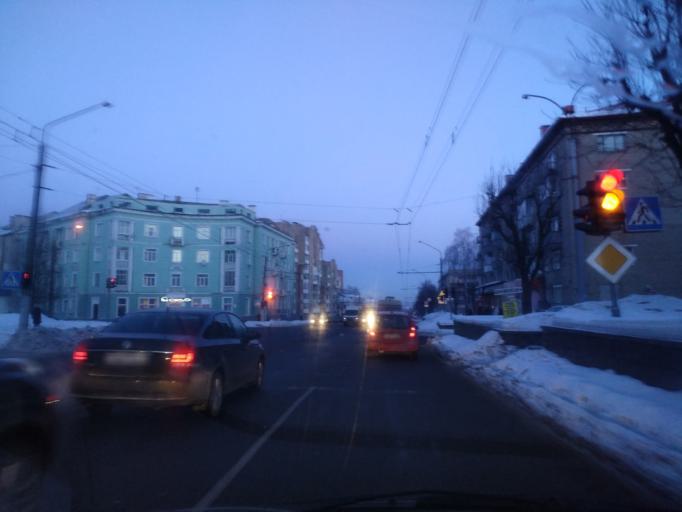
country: BY
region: Mogilev
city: Mahilyow
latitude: 53.8938
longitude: 30.3129
